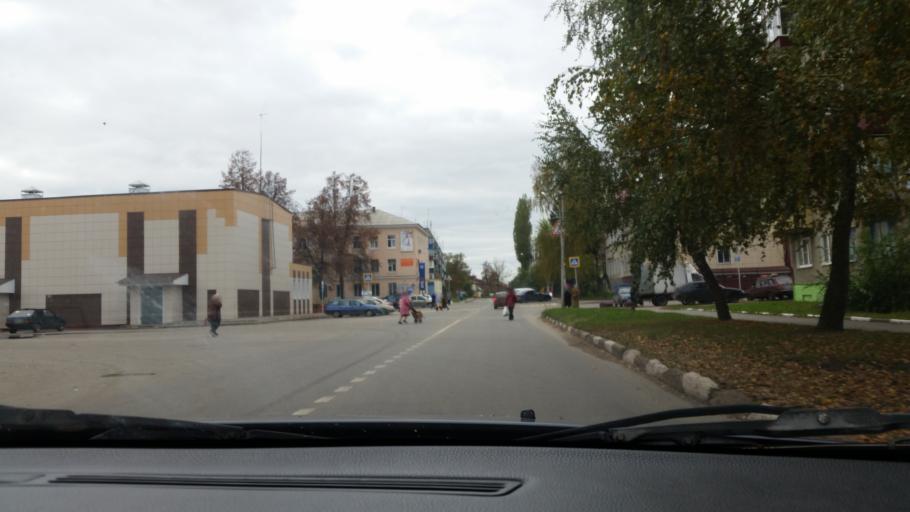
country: RU
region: Lipetsk
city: Gryazi
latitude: 52.4912
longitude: 39.9558
